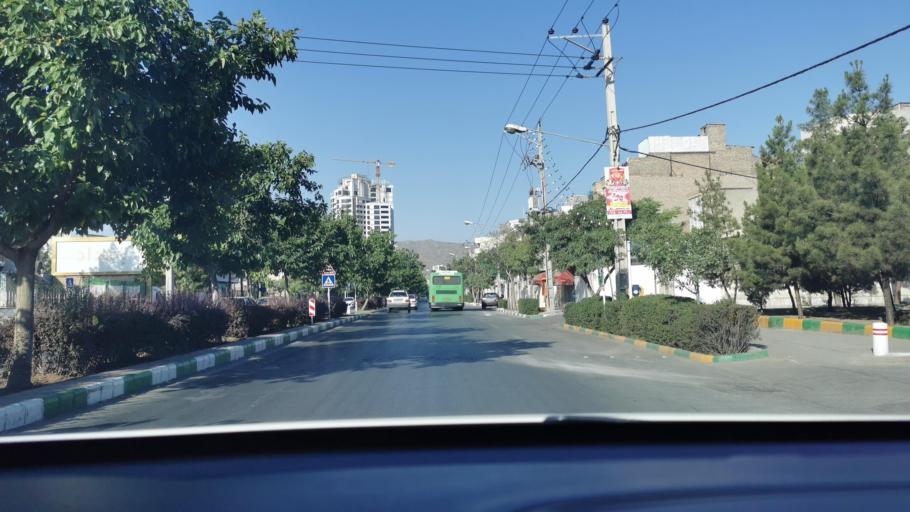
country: IR
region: Razavi Khorasan
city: Mashhad
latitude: 36.3175
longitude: 59.5219
